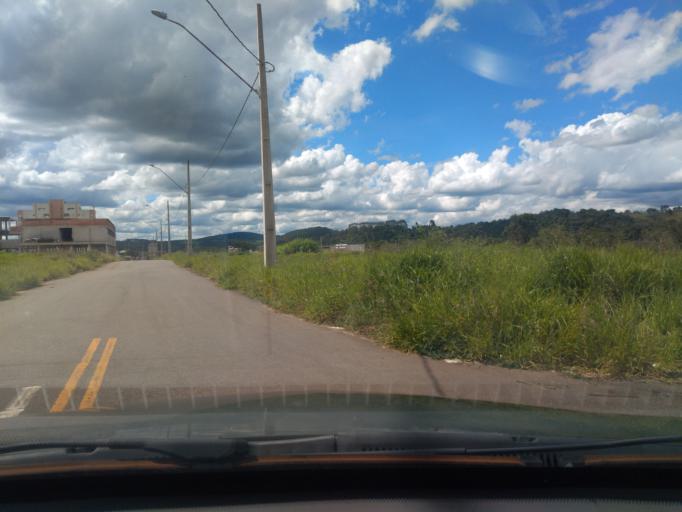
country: BR
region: Minas Gerais
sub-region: Tres Coracoes
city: Tres Coracoes
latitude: -21.6787
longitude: -45.2628
